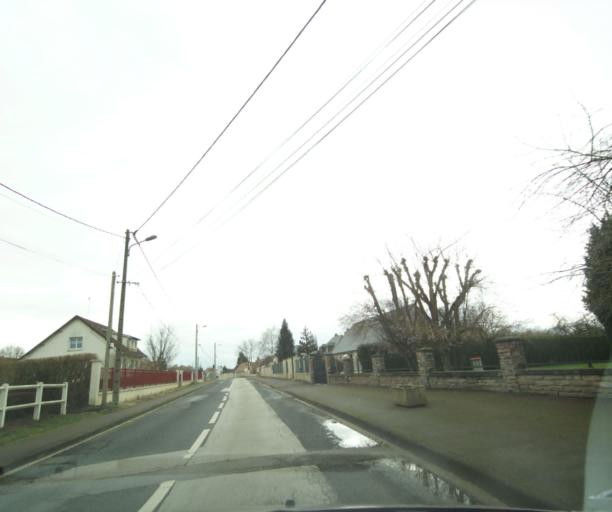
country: FR
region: Picardie
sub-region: Departement de l'Oise
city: Noyon
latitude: 49.5907
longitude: 2.9931
